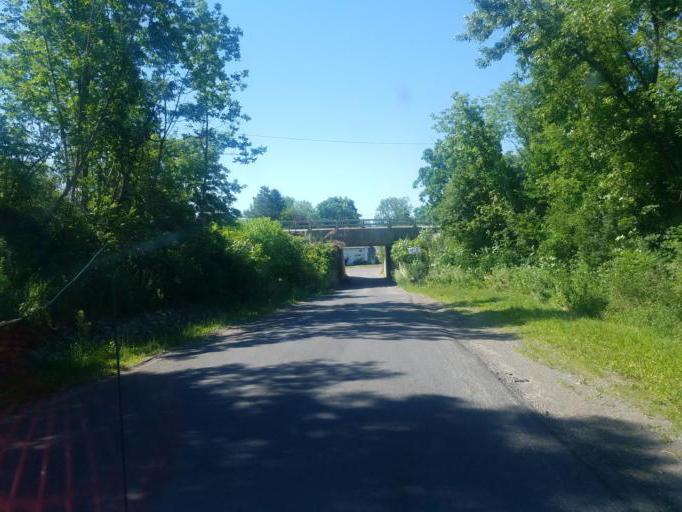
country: US
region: New York
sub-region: Wayne County
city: Newark
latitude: 43.0597
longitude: -77.0452
